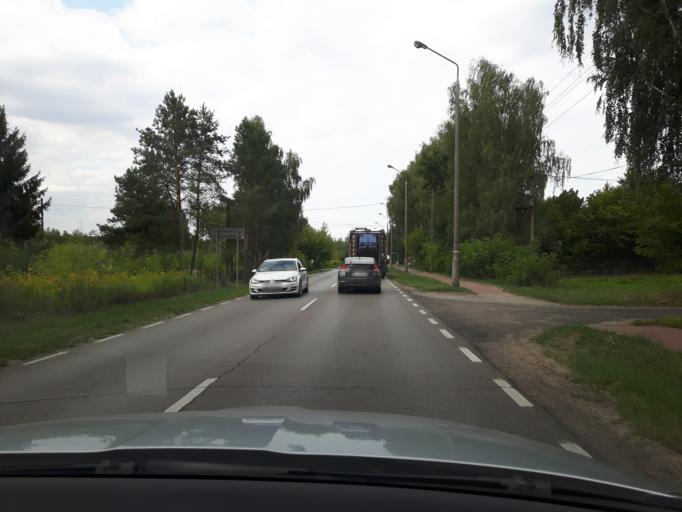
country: PL
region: Masovian Voivodeship
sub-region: Powiat legionowski
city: Stanislawow Pierwszy
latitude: 52.3909
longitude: 21.0325
